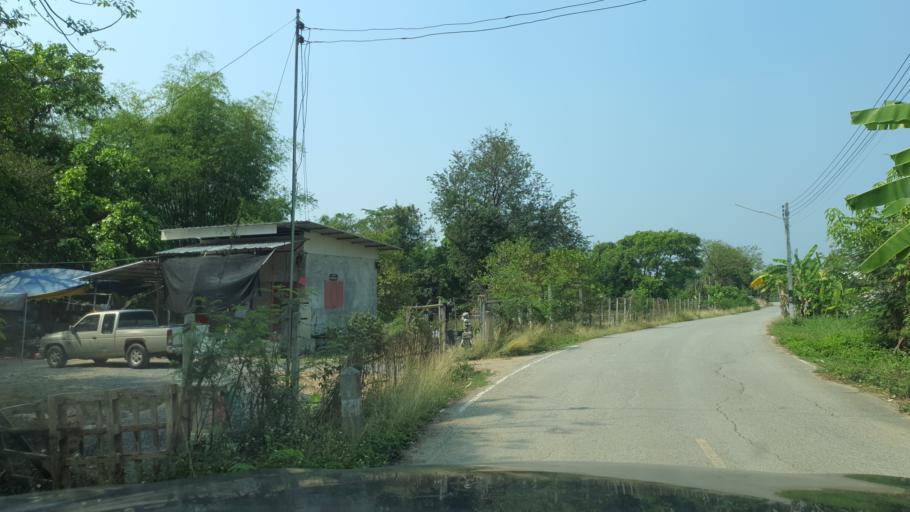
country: TH
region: Chiang Mai
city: Saraphi
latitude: 18.7307
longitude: 99.0685
